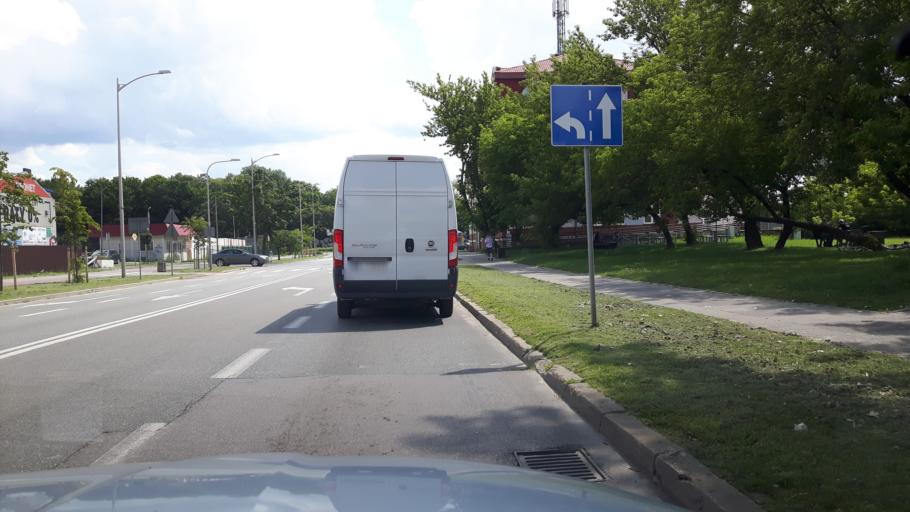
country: PL
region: Masovian Voivodeship
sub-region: Powiat wyszkowski
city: Wyszkow
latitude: 52.5935
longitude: 21.4525
